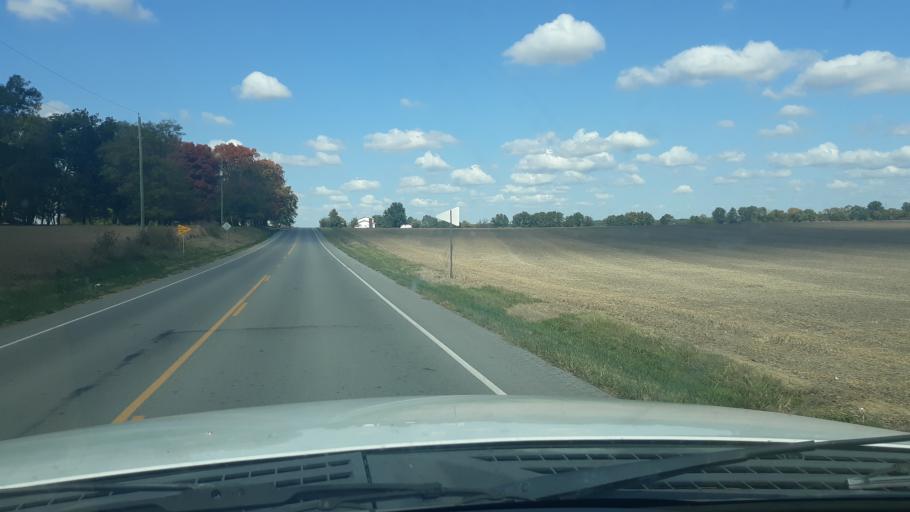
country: US
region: Illinois
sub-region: Saline County
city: Eldorado
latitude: 37.7912
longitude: -88.4848
